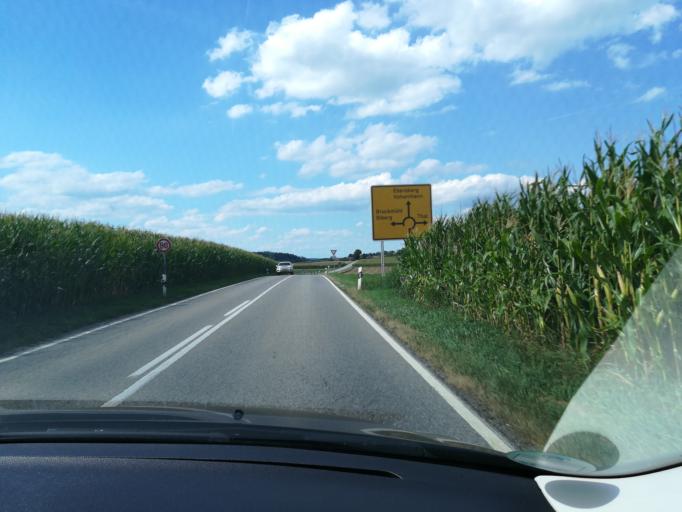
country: DE
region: Bavaria
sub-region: Upper Bavaria
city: Assling
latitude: 47.9647
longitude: 11.9638
